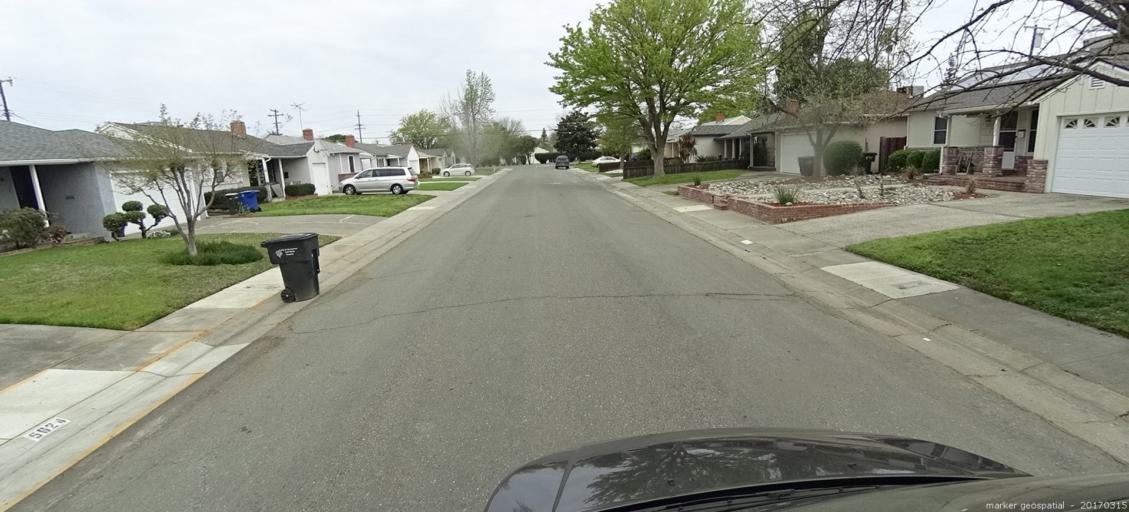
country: US
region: California
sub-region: Sacramento County
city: Parkway
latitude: 38.5236
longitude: -121.4929
